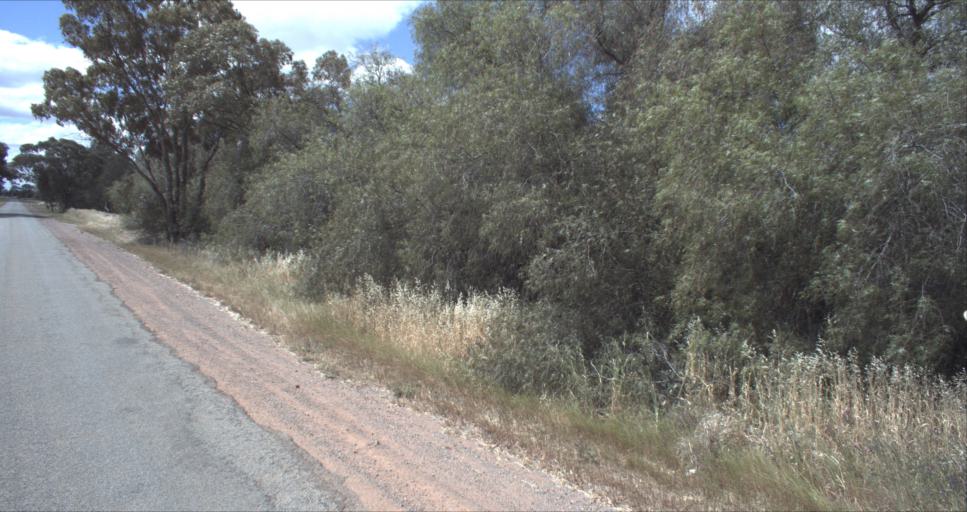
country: AU
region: New South Wales
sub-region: Leeton
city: Leeton
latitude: -34.5877
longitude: 146.3957
